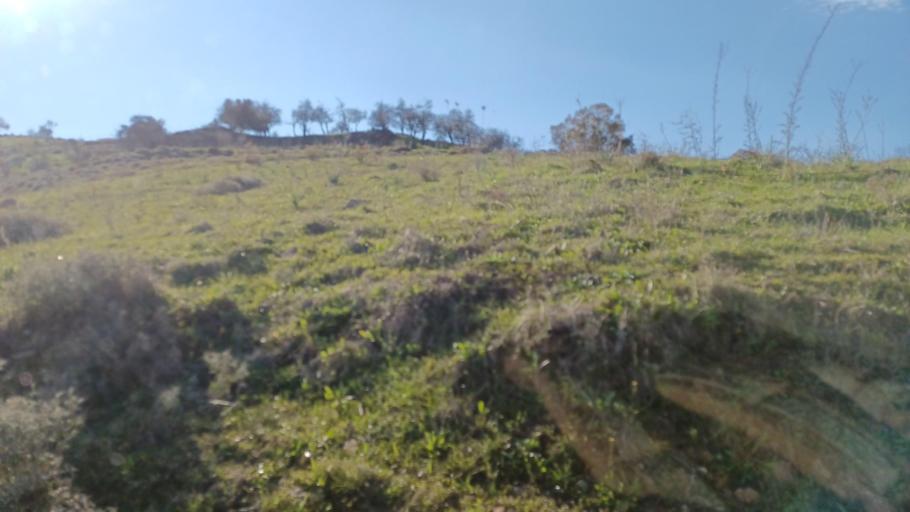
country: CY
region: Limassol
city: Pachna
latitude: 34.8165
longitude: 32.6509
